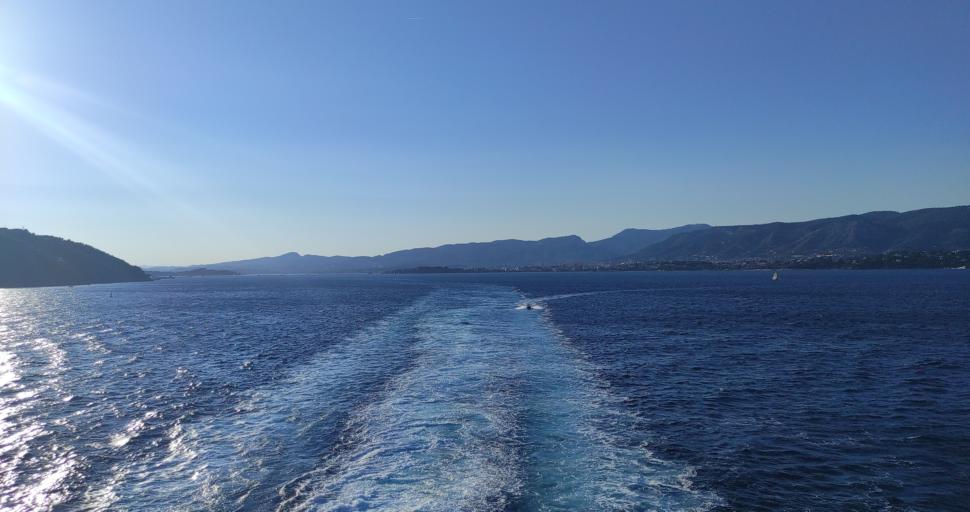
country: FR
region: Provence-Alpes-Cote d'Azur
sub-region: Departement du Var
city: Saint-Mandrier-sur-Mer
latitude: 43.0733
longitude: 5.9676
